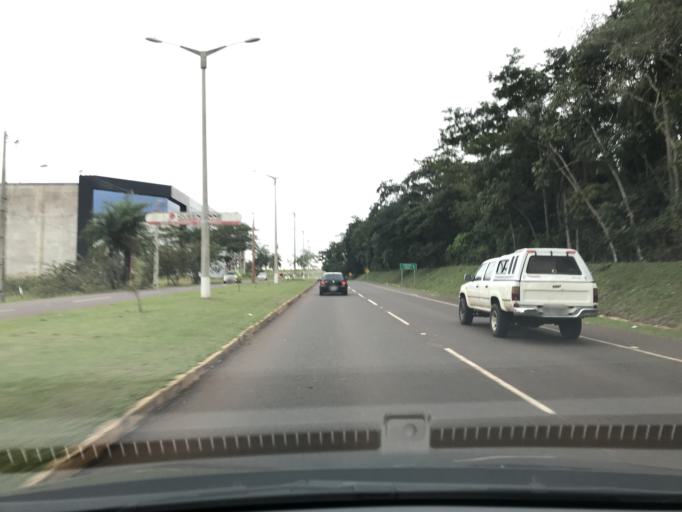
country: PY
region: Canindeyu
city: Salto del Guaira
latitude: -24.0093
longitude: -54.3239
